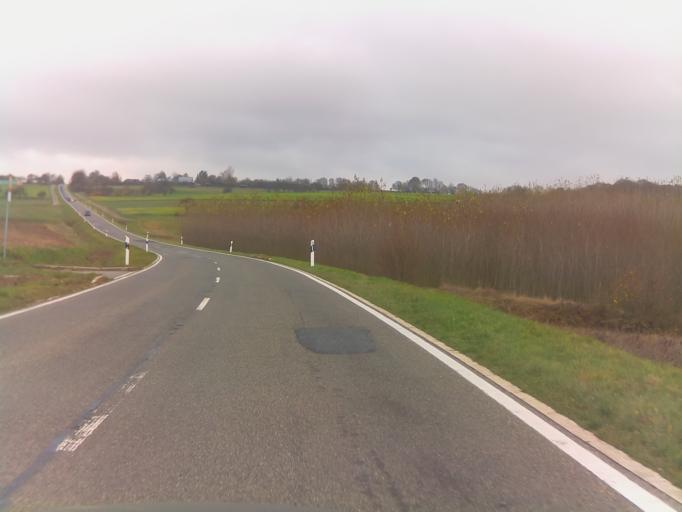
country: DE
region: Baden-Wuerttemberg
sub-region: Karlsruhe Region
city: Neckargerach
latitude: 49.4198
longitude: 9.0876
